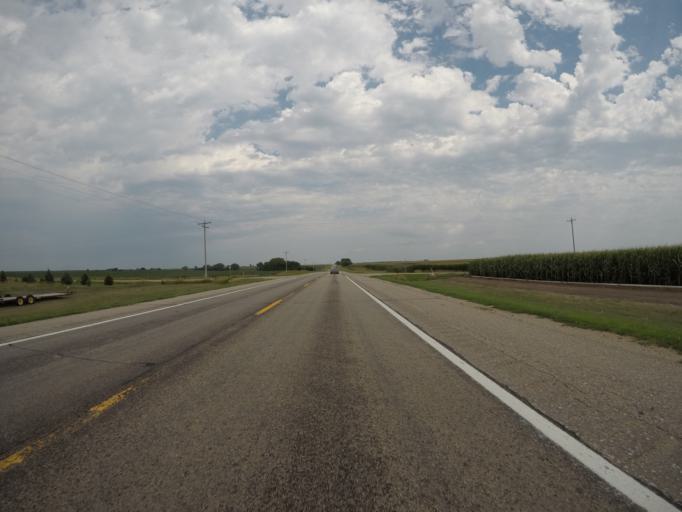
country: US
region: Nebraska
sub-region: Clay County
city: Harvard
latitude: 40.5827
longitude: -98.0713
